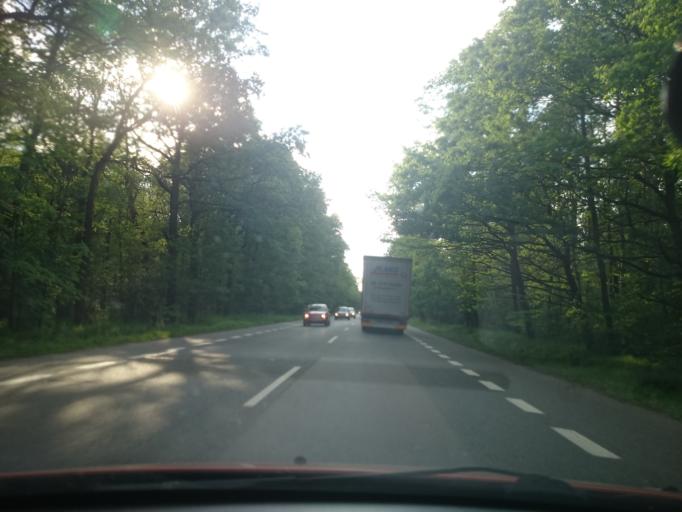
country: PL
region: Opole Voivodeship
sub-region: Powiat opolski
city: Chrzastowice
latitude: 50.6359
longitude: 18.0096
